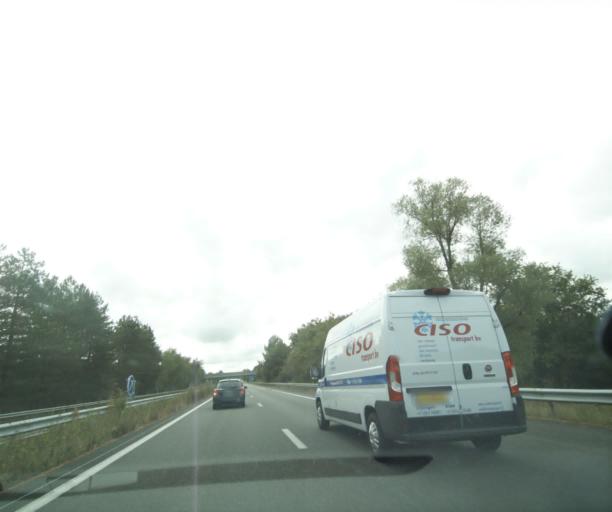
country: FR
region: Poitou-Charentes
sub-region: Departement de la Charente-Maritime
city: Saint-Genis-de-Saintonge
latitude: 45.4495
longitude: -0.6123
